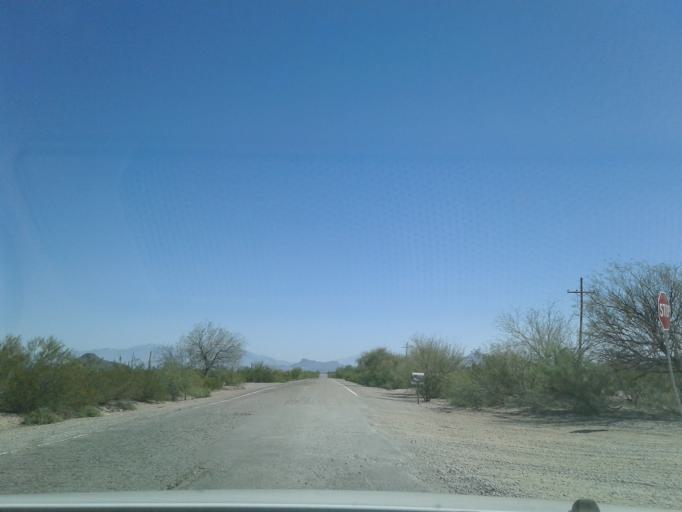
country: US
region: Arizona
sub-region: Pima County
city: Avra Valley
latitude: 32.3735
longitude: -111.4539
